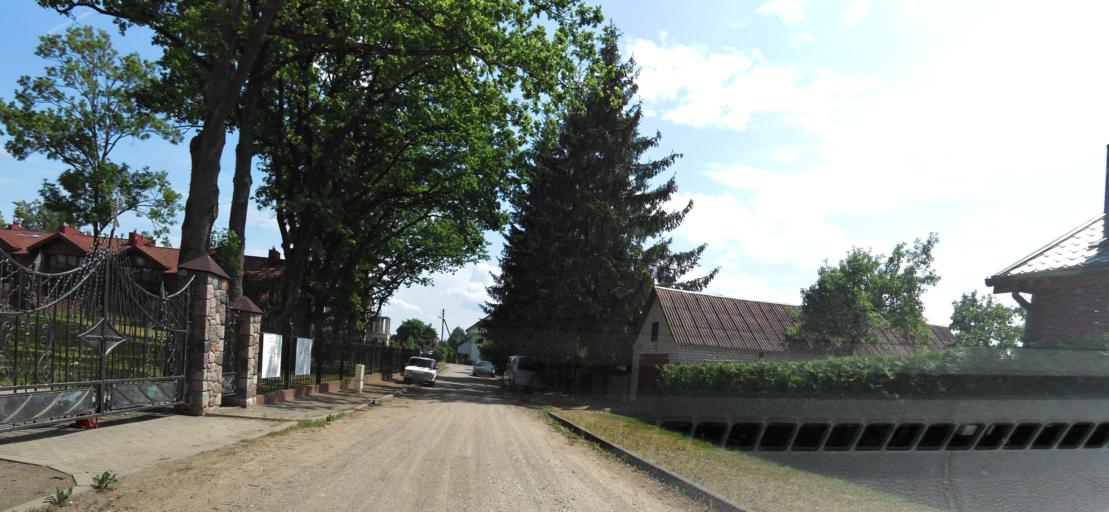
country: LT
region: Vilnius County
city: Pasilaiciai
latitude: 54.7608
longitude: 25.2069
